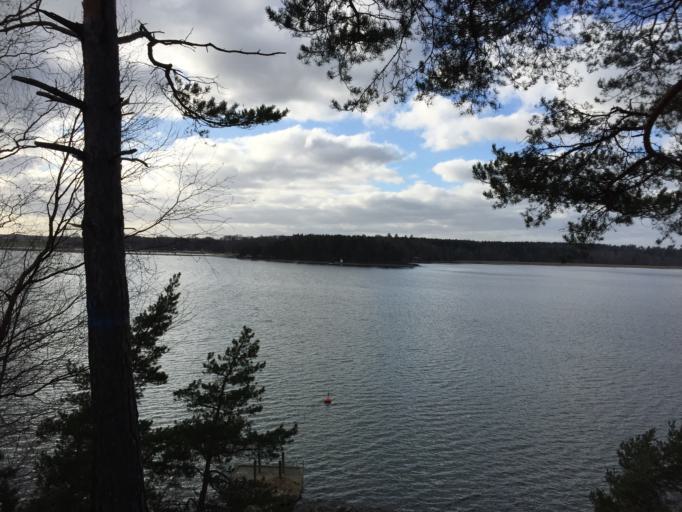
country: SE
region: Stockholm
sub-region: Sodertalje Kommun
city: Pershagen
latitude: 59.0557
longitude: 17.6933
